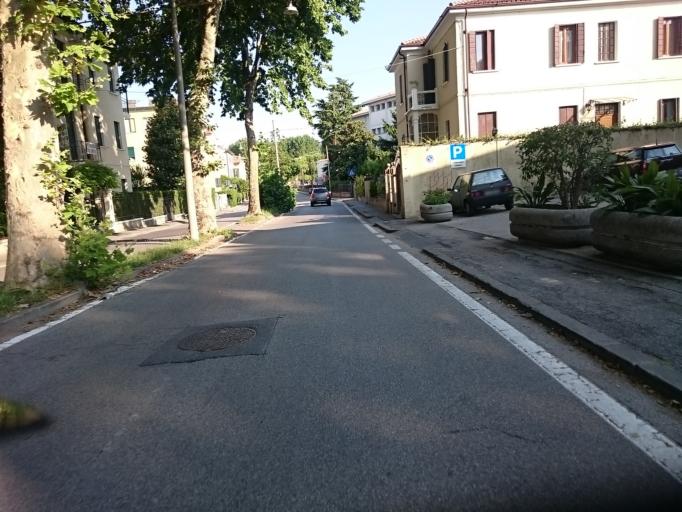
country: IT
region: Veneto
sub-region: Provincia di Padova
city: Padova
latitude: 45.3959
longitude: 11.8827
